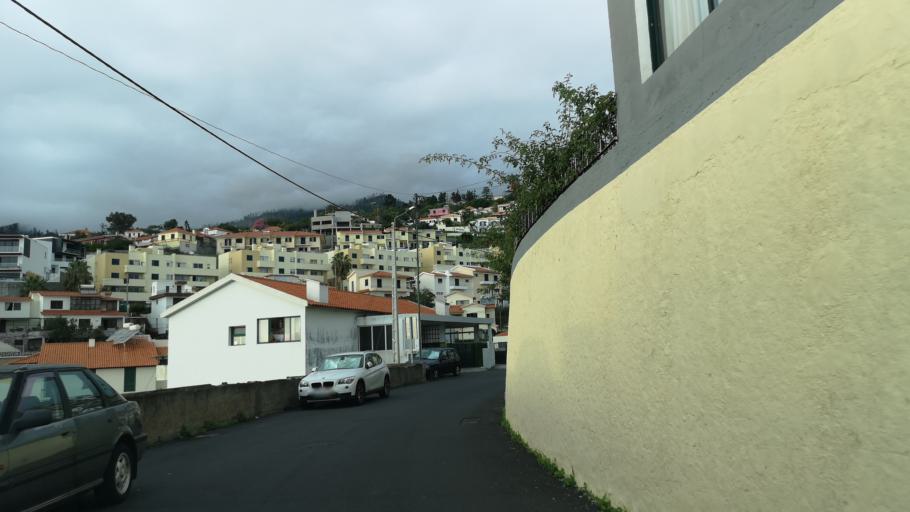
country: PT
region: Madeira
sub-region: Funchal
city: Nossa Senhora do Monte
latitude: 32.6574
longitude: -16.8953
